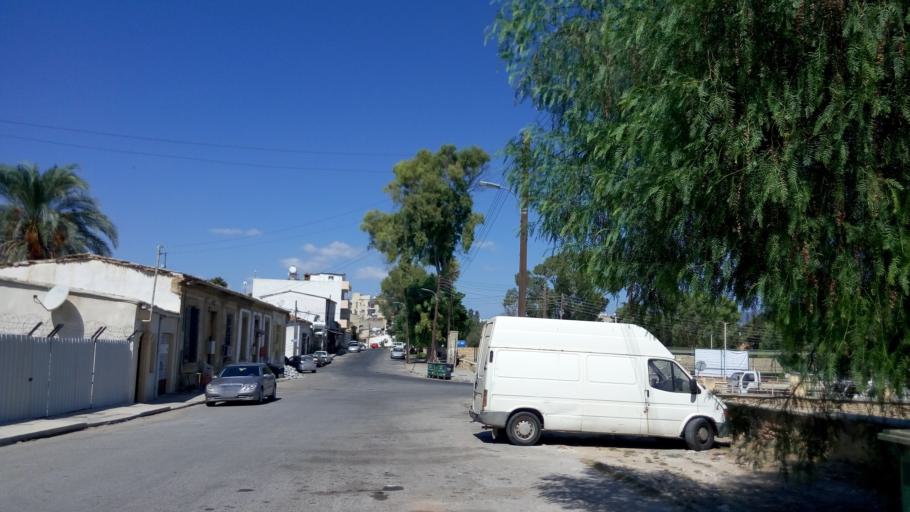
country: CY
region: Lefkosia
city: Nicosia
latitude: 35.1793
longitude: 33.3700
